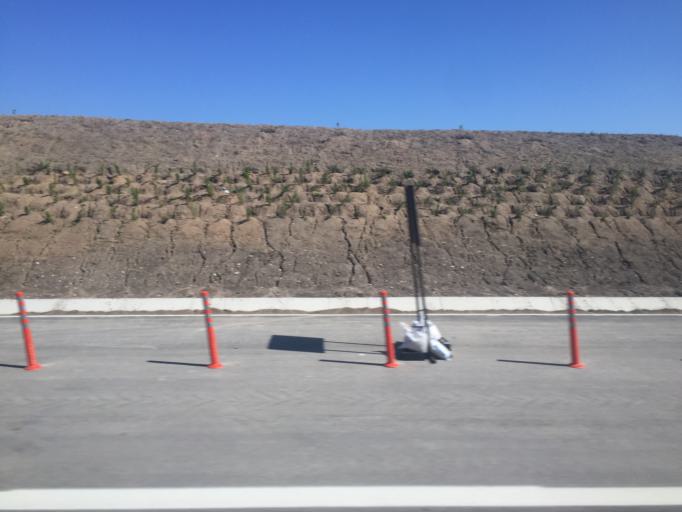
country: TR
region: Bursa
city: Mahmudiye
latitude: 40.2648
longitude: 28.6612
